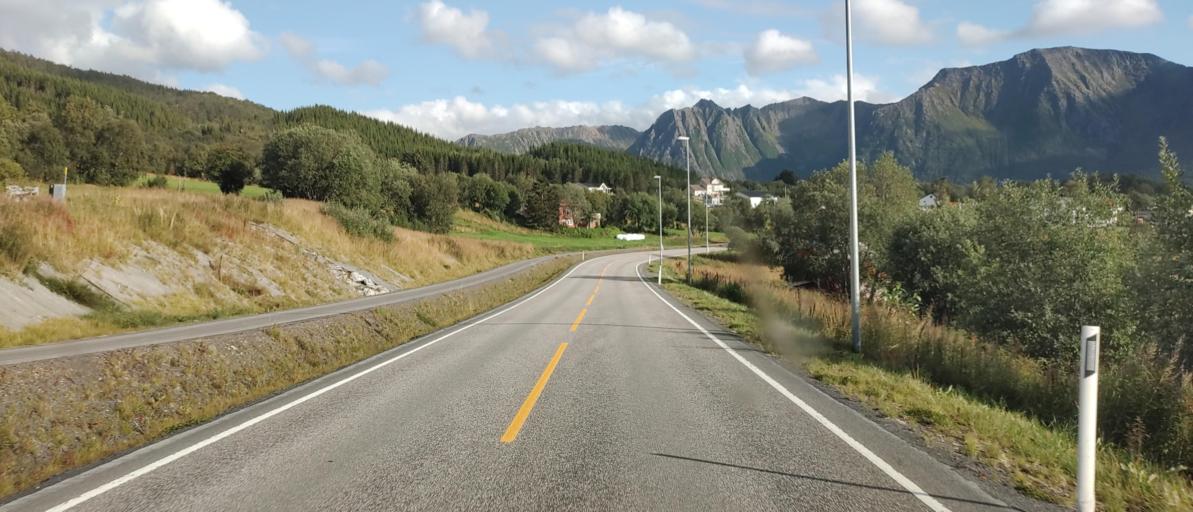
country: NO
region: Nordland
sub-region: Sortland
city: Sortland
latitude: 68.7485
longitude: 15.5000
